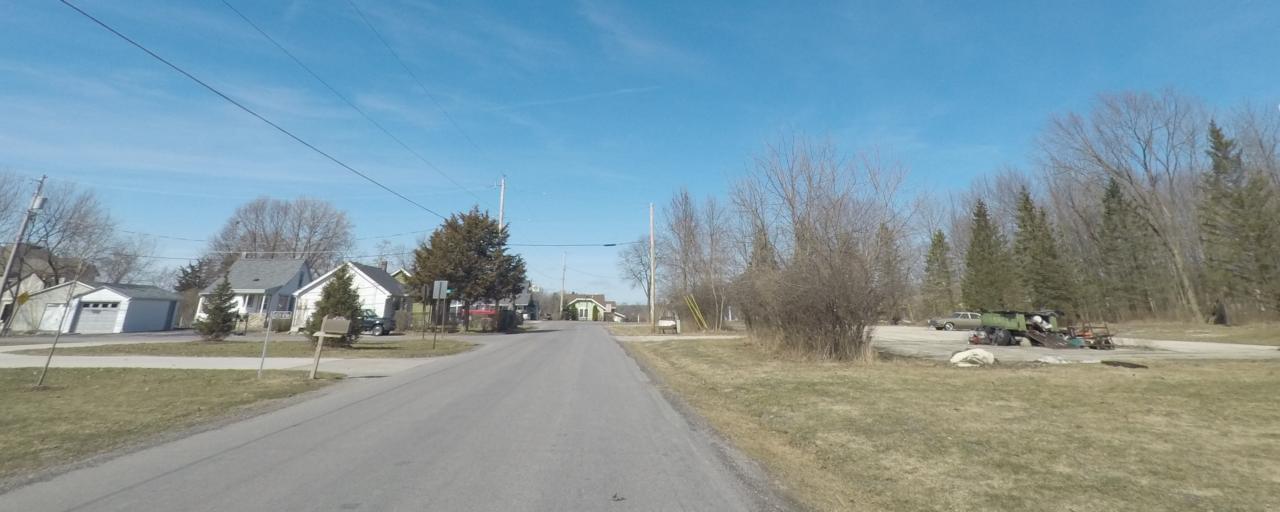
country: US
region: Wisconsin
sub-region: Waukesha County
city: Merton
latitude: 43.1609
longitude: -88.3213
